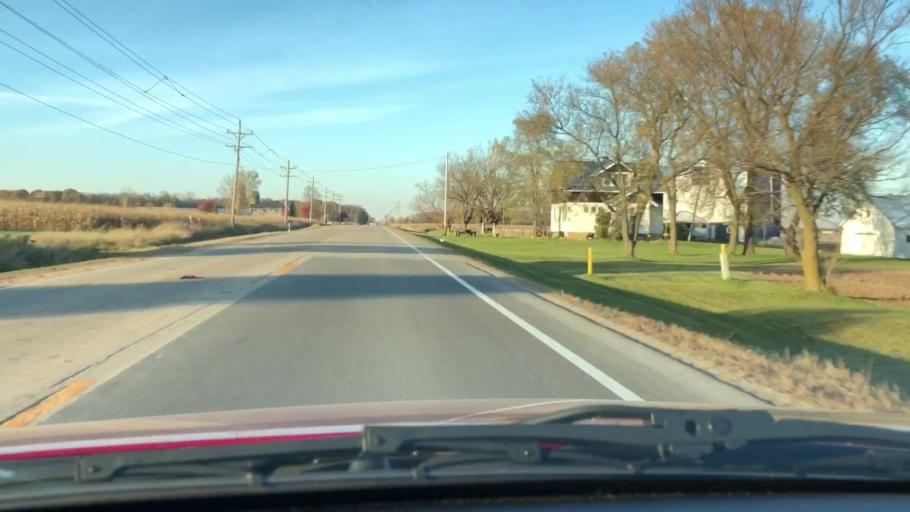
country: US
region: Wisconsin
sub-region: Outagamie County
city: Seymour
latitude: 44.4512
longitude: -88.2912
